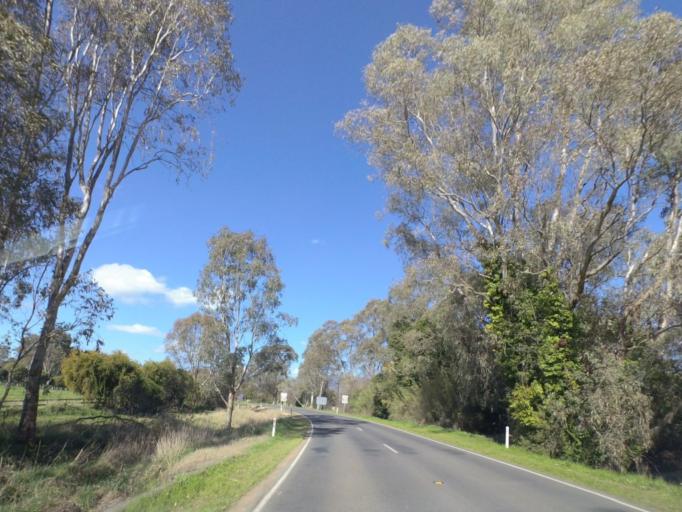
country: AU
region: Victoria
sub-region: Murrindindi
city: Alexandra
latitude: -37.2540
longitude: 145.7904
